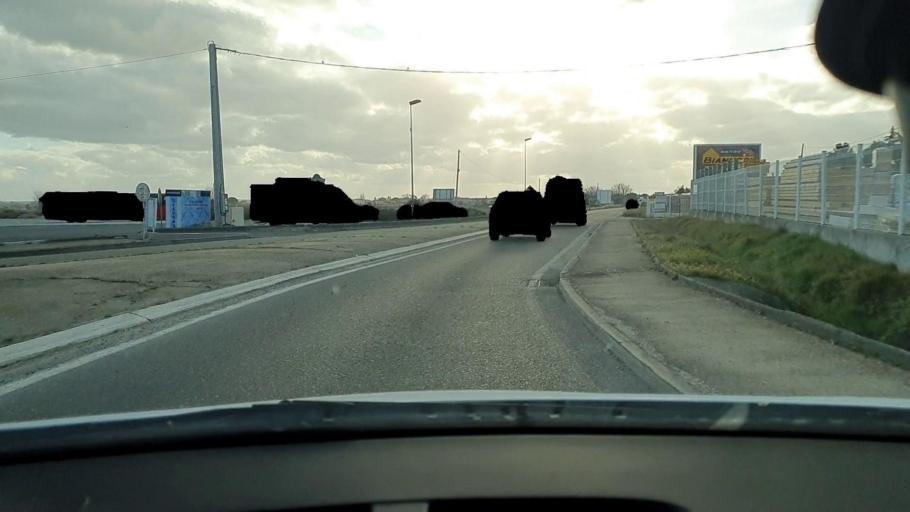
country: FR
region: Languedoc-Roussillon
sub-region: Departement du Gard
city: Saint-Gervasy
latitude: 43.8749
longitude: 4.4659
